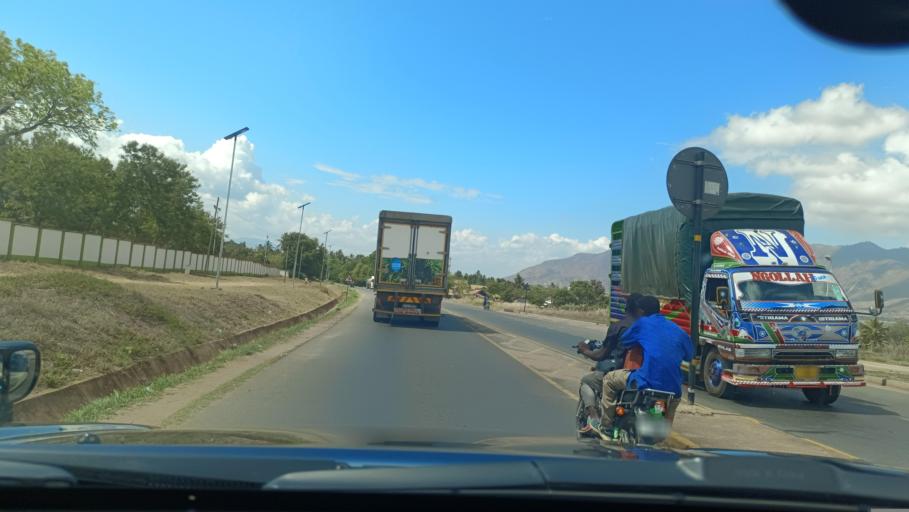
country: TZ
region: Morogoro
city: Morogoro
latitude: -6.8109
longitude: 37.6516
